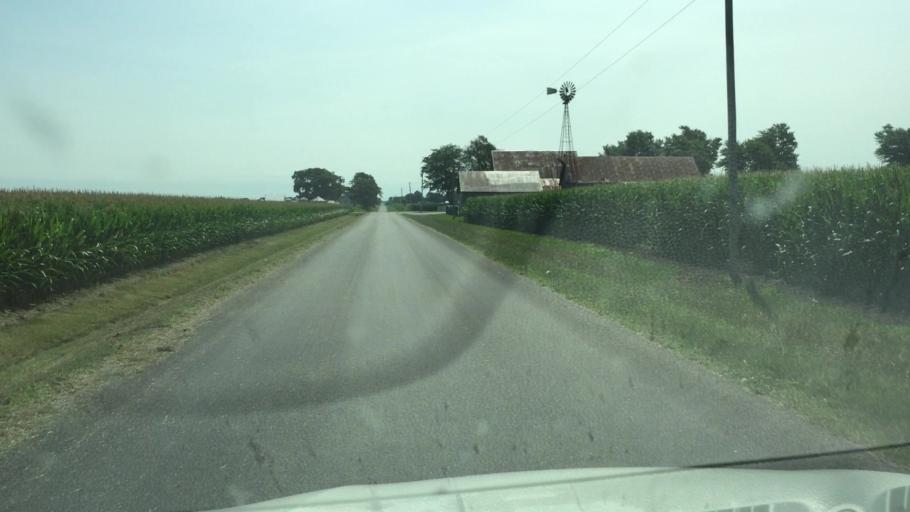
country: US
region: Illinois
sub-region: Hancock County
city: Nauvoo
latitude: 40.5072
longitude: -91.3114
